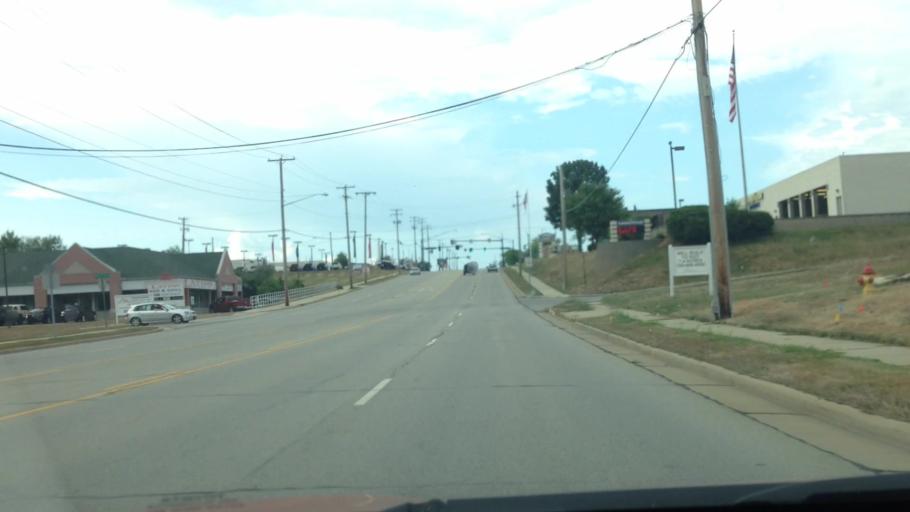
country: US
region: Ohio
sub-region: Summit County
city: Green
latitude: 40.9767
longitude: -81.4928
